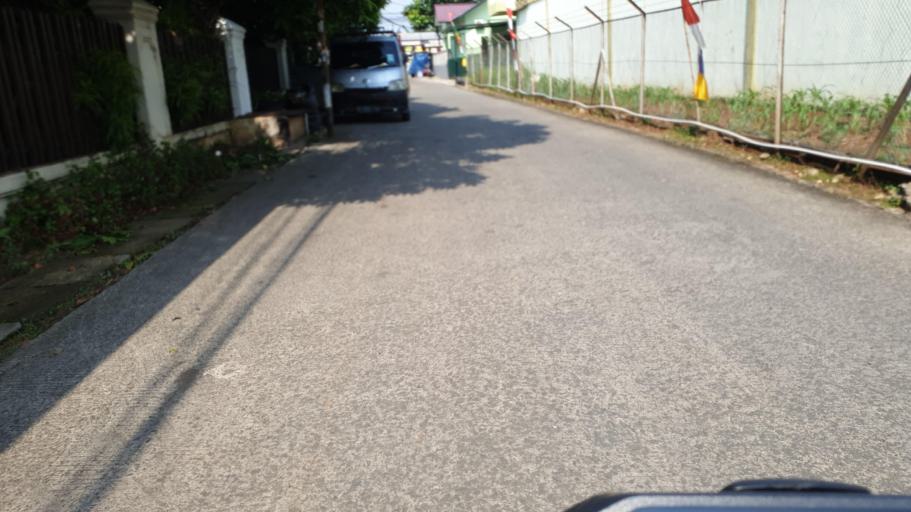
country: ID
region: West Java
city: Depok
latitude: -6.3711
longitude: 106.8419
